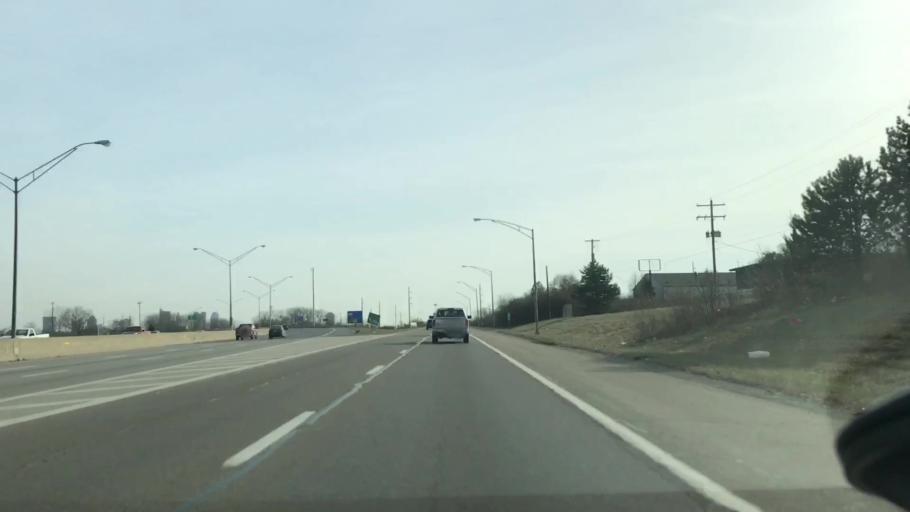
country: US
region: Ohio
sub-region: Franklin County
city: Upper Arlington
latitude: 39.9681
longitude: -83.0648
